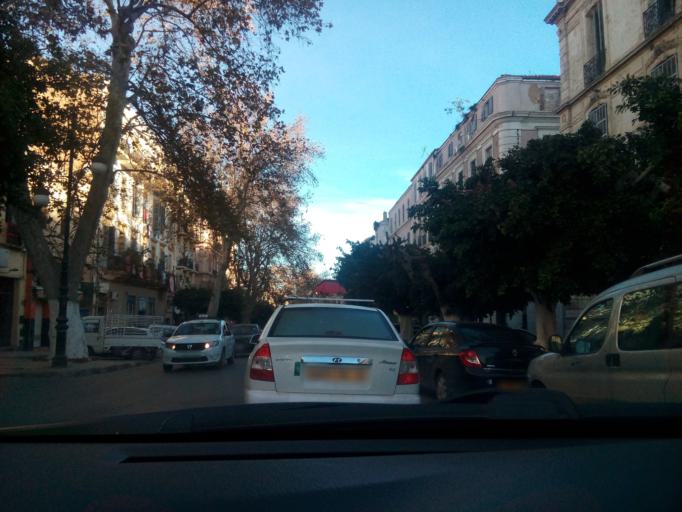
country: DZ
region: Oran
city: Oran
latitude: 35.7030
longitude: -0.6529
